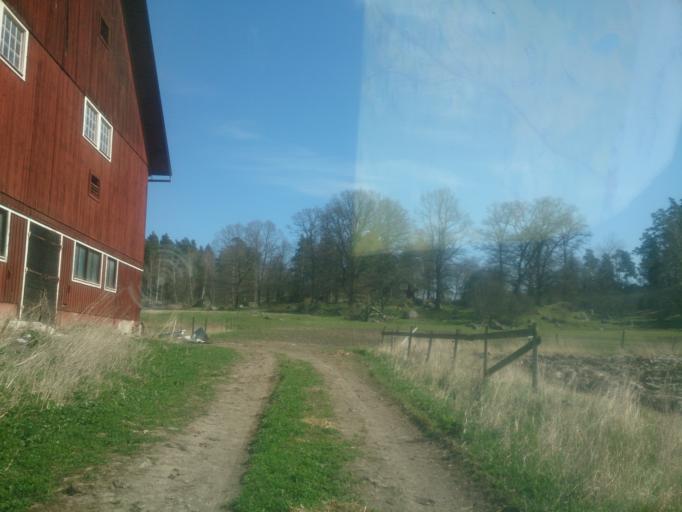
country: SE
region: OEstergoetland
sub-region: Linkopings Kommun
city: Sturefors
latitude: 58.3039
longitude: 15.8598
